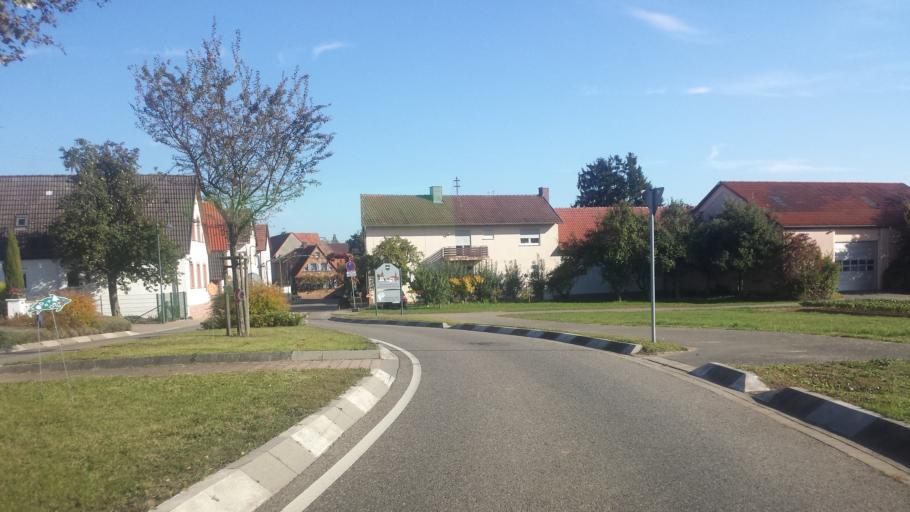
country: DE
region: Rheinland-Pfalz
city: Kleinfischlingen
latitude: 49.2640
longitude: 8.1836
